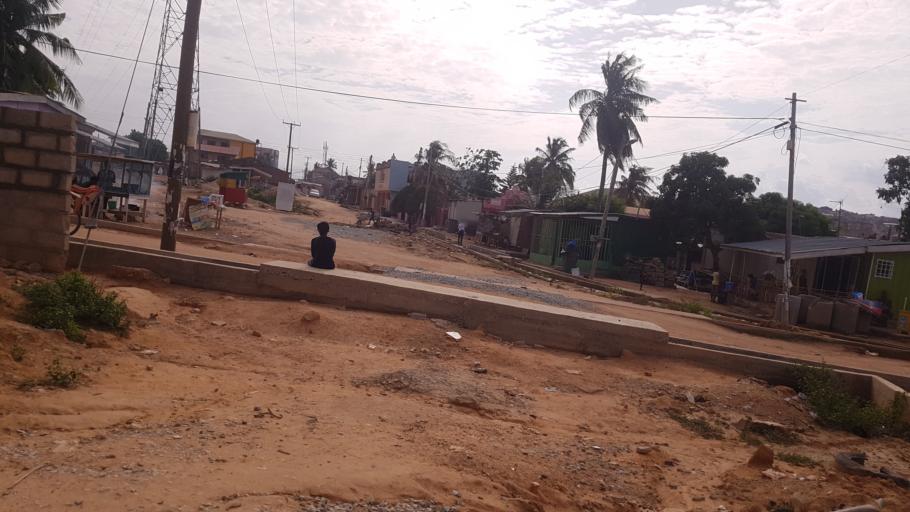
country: GH
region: Greater Accra
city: Gbawe
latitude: 5.5516
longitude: -0.3433
